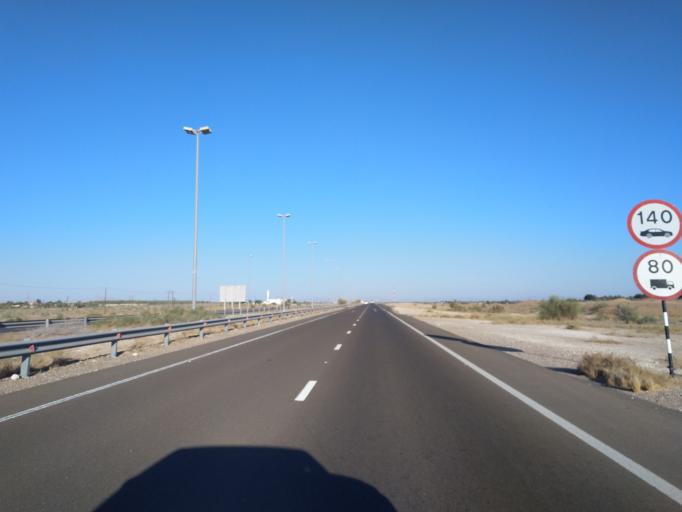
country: OM
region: Al Buraimi
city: Al Buraymi
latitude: 24.5385
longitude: 55.6111
